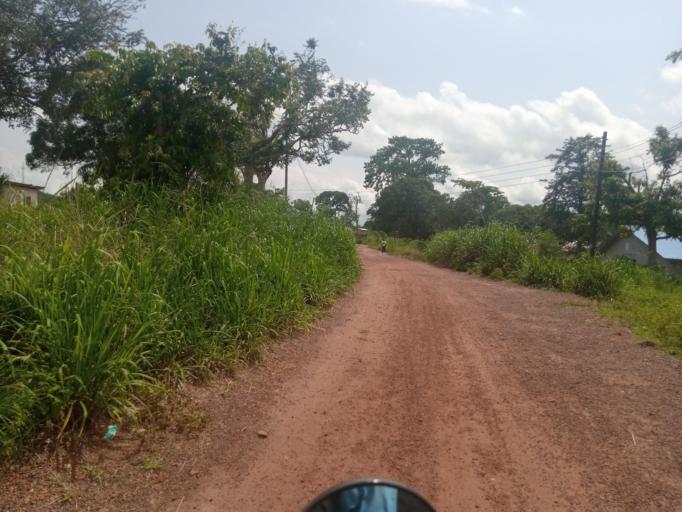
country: SL
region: Southern Province
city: Bo
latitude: 7.9646
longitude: -11.7518
